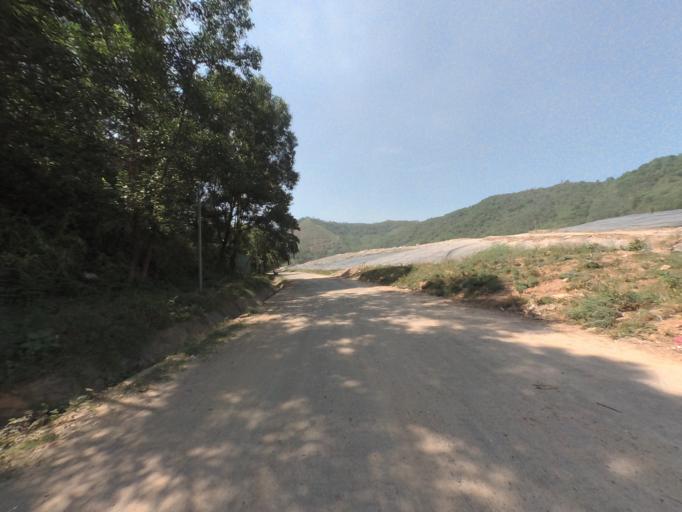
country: VN
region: Da Nang
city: Lien Chieu
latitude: 16.0443
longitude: 108.1422
